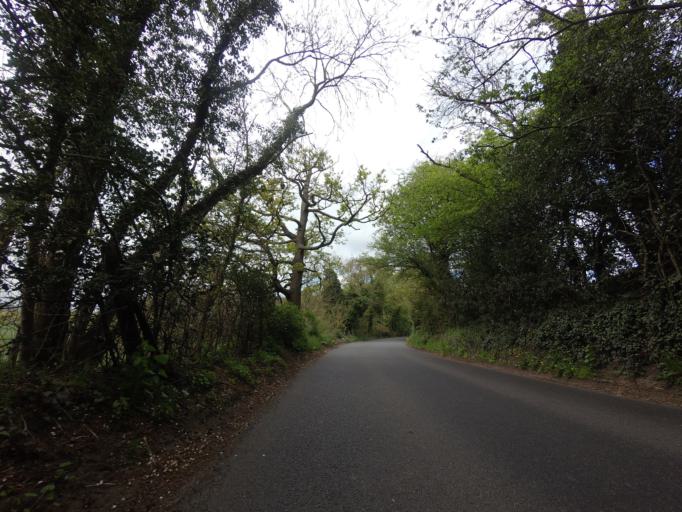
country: GB
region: England
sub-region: Greater London
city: Orpington
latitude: 51.3828
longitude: 0.1288
